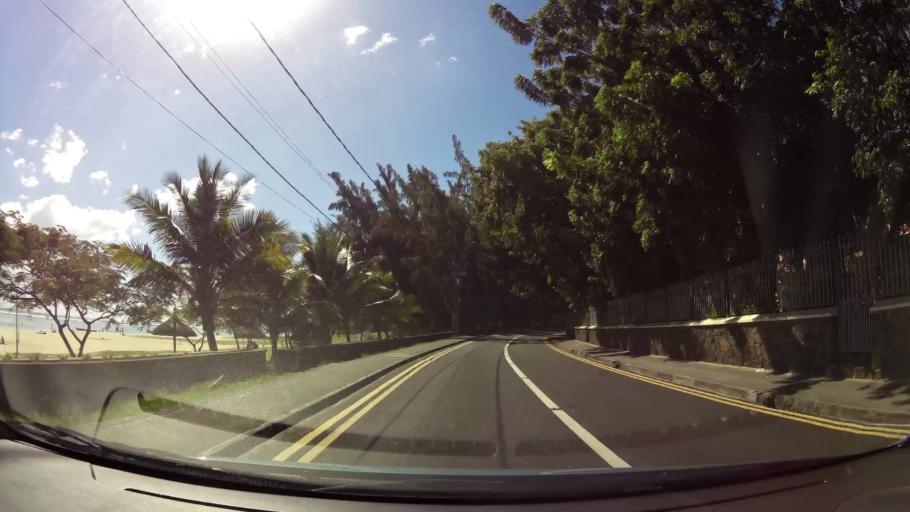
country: MU
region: Black River
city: Flic en Flac
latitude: -20.2796
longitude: 57.3666
